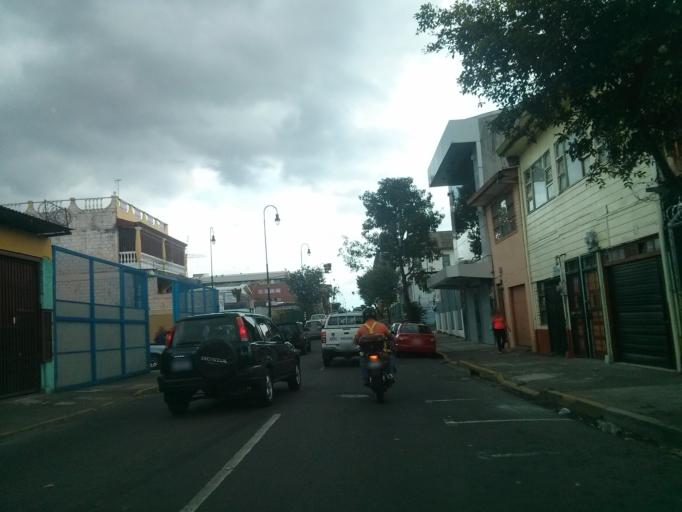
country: CR
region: San Jose
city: San Jose
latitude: 9.9261
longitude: -84.0771
